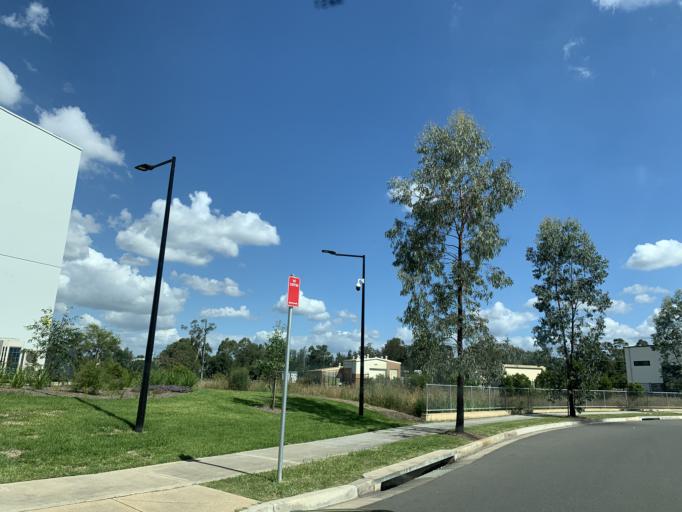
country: AU
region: New South Wales
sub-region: Penrith Municipality
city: Penrith
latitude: -33.7303
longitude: 150.7059
